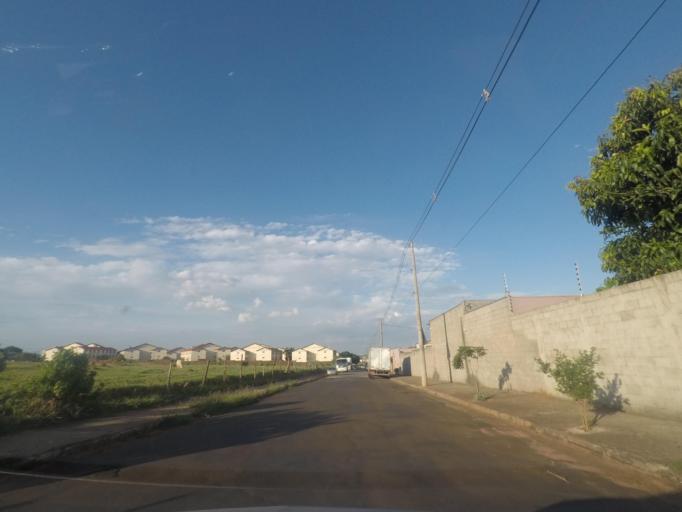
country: BR
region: Sao Paulo
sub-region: Sumare
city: Sumare
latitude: -22.8191
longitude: -47.2862
